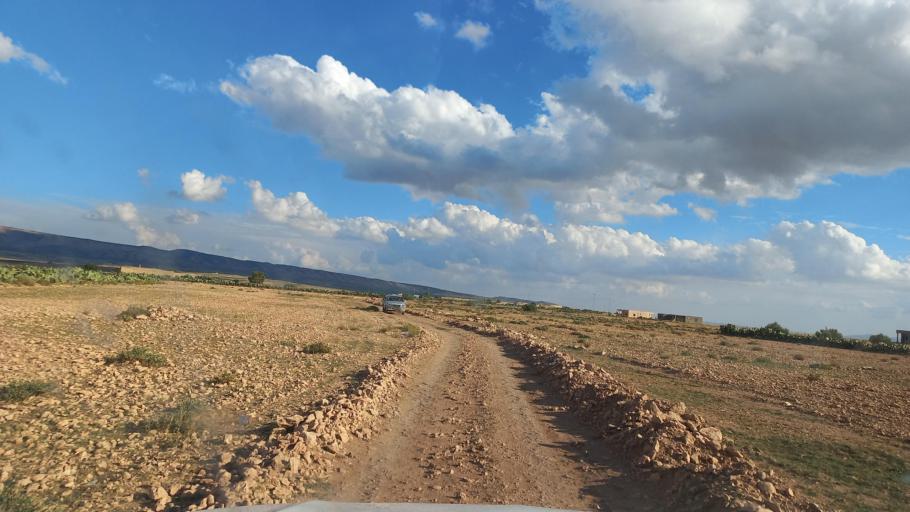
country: TN
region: Al Qasrayn
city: Sbiba
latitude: 35.3852
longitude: 9.0688
